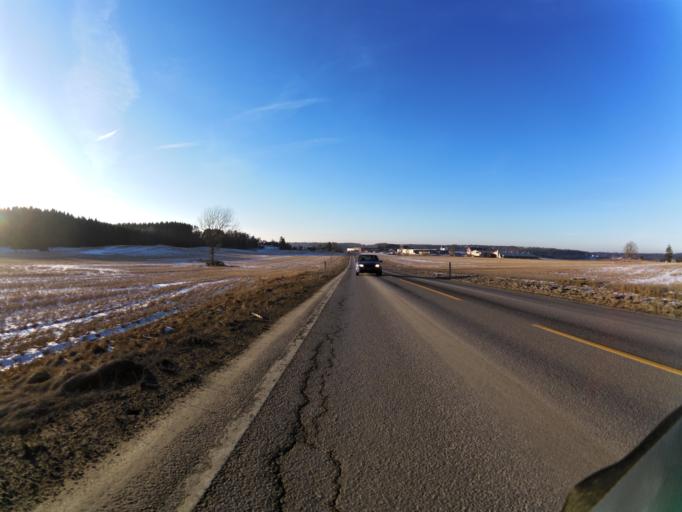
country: NO
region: Ostfold
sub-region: Fredrikstad
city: Lervik
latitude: 59.2618
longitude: 10.8158
